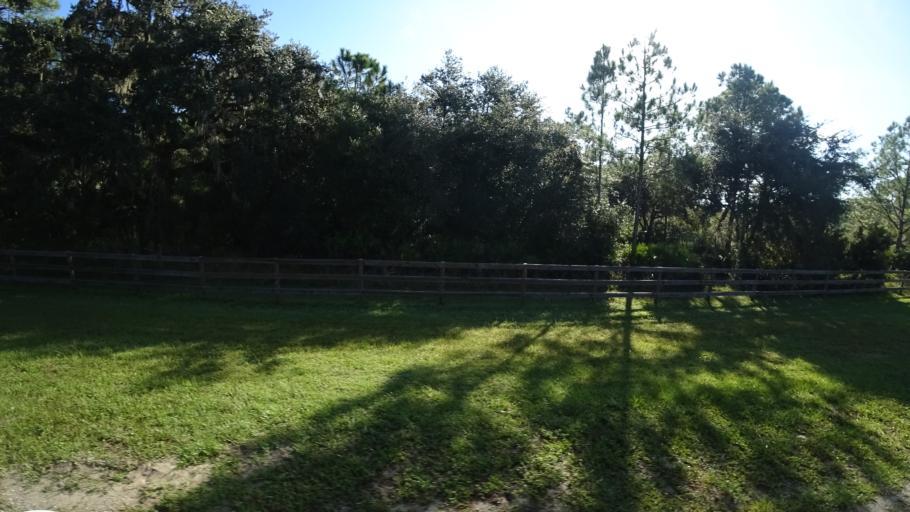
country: US
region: Florida
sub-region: Sarasota County
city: The Meadows
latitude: 27.4199
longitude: -82.3437
